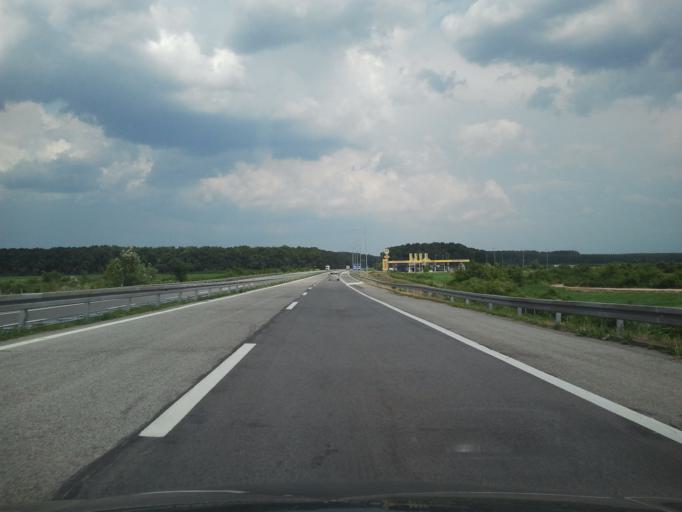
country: RS
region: Autonomna Pokrajina Vojvodina
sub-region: Sremski Okrug
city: Sid
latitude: 45.0478
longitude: 19.2192
